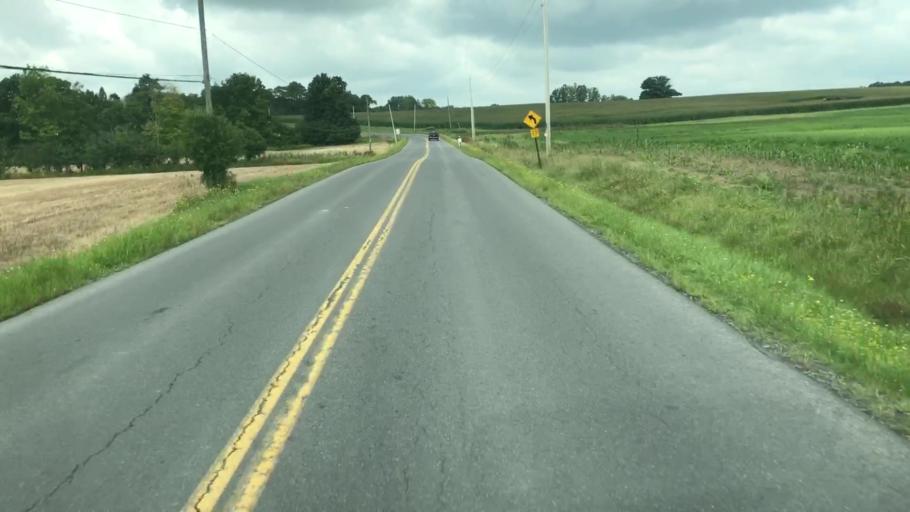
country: US
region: New York
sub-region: Cayuga County
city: Melrose Park
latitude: 42.9190
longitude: -76.5242
